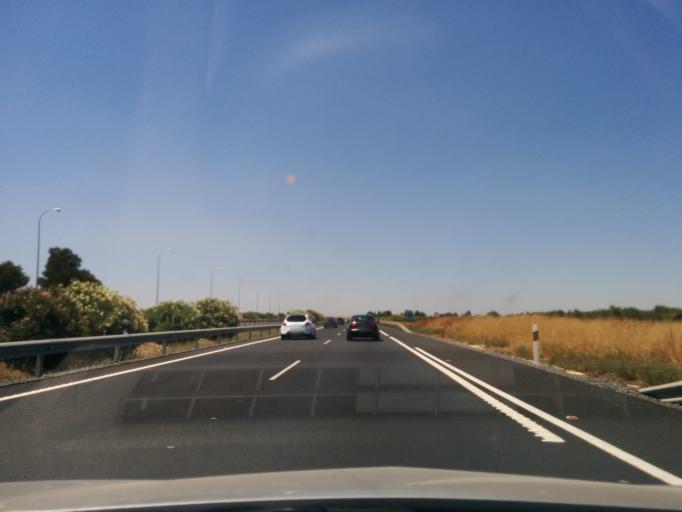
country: ES
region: Andalusia
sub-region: Provincia de Huelva
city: San Juan del Puerto
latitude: 37.3330
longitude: -6.7969
